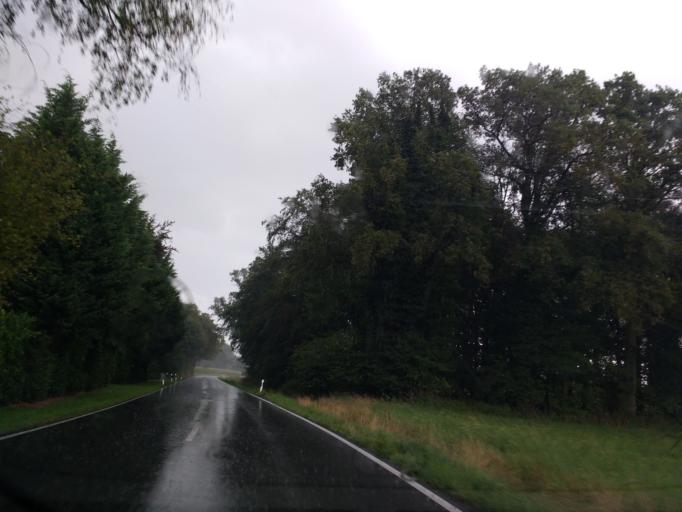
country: DE
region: North Rhine-Westphalia
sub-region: Regierungsbezirk Munster
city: Lienen
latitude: 52.1124
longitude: 7.9373
